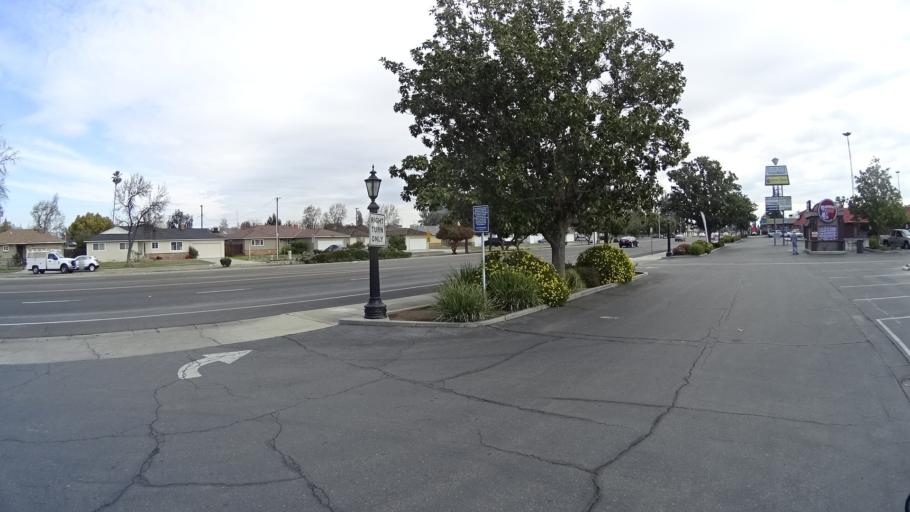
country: US
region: California
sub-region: Fresno County
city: Fresno
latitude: 36.8155
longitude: -119.7745
